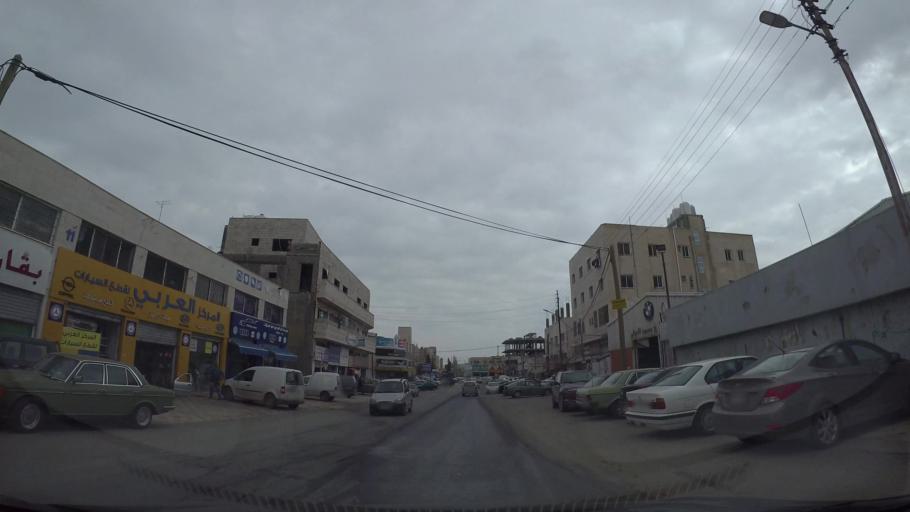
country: JO
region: Amman
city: Wadi as Sir
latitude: 31.9440
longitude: 35.8440
